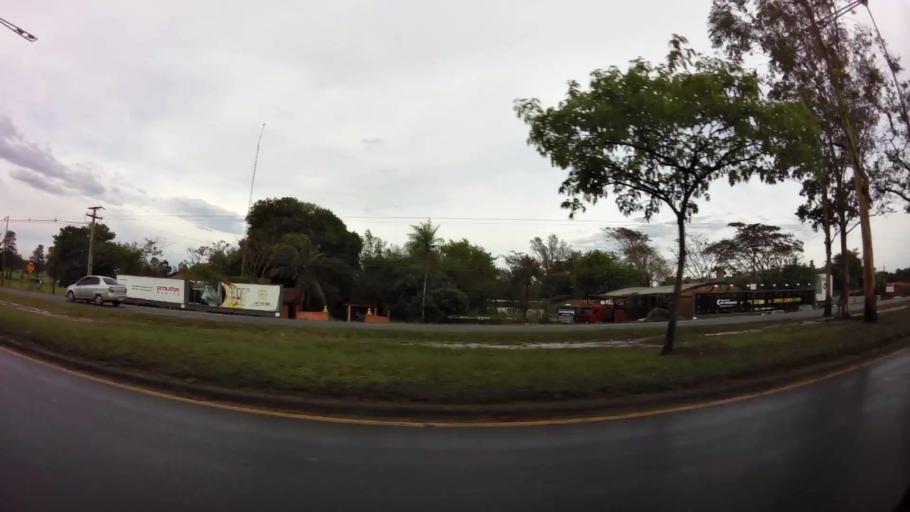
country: PY
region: Central
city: Fernando de la Mora
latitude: -25.2569
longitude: -57.5142
